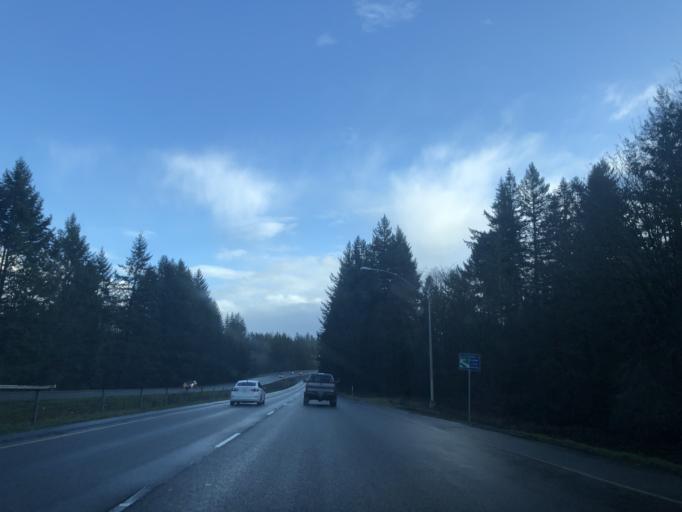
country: US
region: Washington
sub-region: Kitsap County
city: Erlands Point-Kitsap Lake
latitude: 47.6000
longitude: -122.7039
